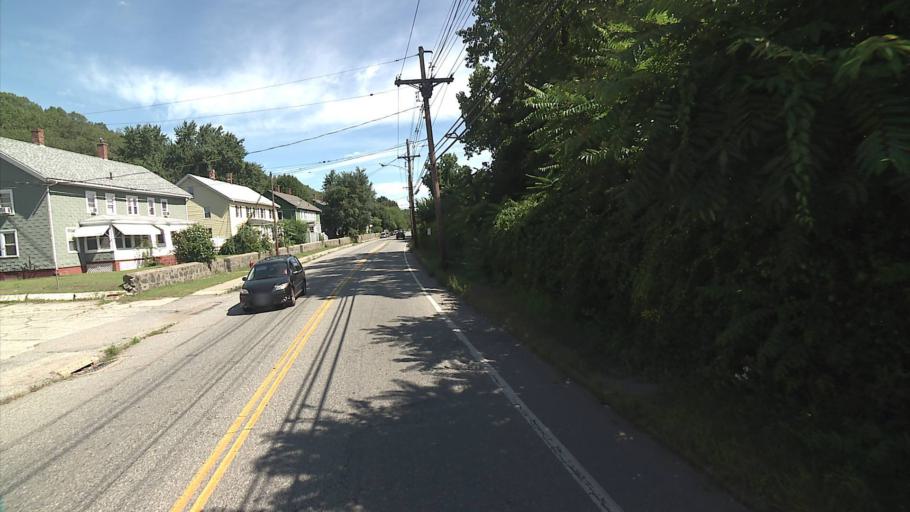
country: US
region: Connecticut
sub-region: New London County
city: Norwich
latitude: 41.5621
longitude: -72.0477
